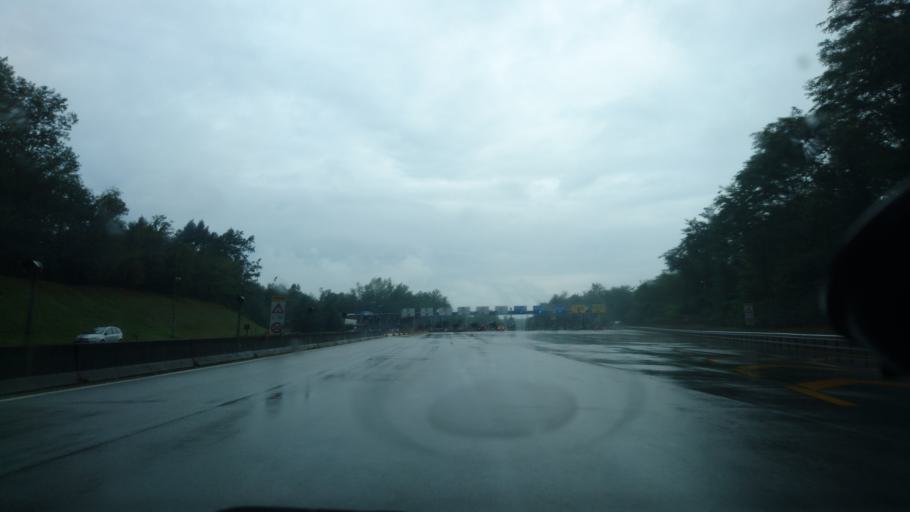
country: IT
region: Piedmont
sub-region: Provincia di Novara
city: Paruzzaro
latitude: 45.7386
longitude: 8.5042
